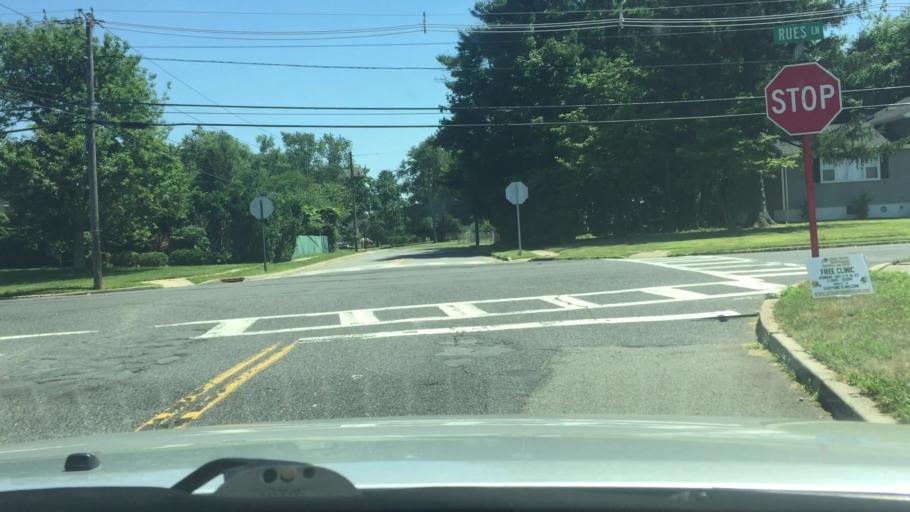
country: US
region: New Jersey
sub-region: Middlesex County
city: East Brunswick
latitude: 40.4188
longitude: -74.3995
